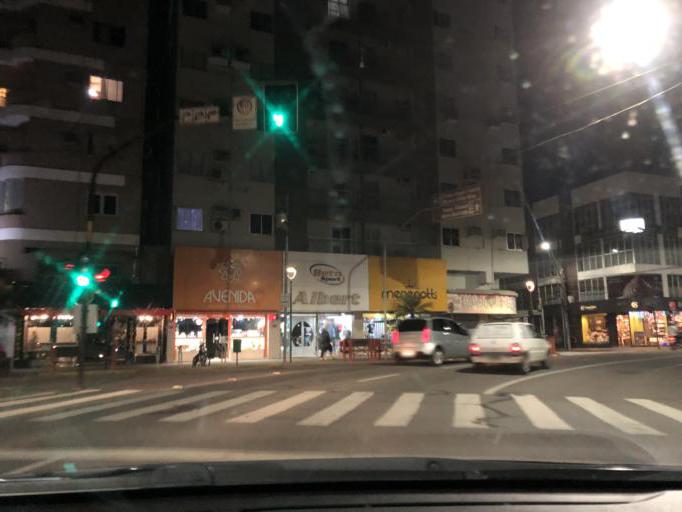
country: BR
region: Santa Catarina
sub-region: Jaragua Do Sul
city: Jaragua do Sul
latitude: -26.4852
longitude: -49.0830
